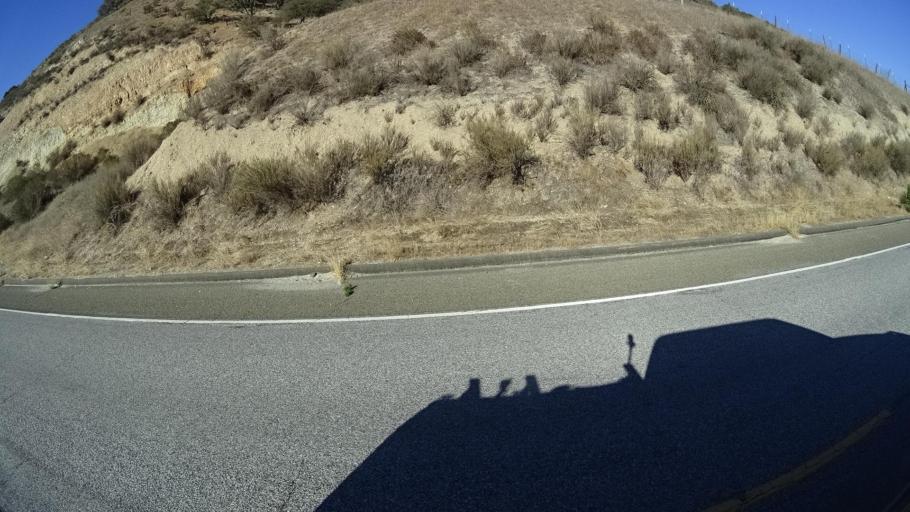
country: US
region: California
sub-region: Monterey County
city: King City
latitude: 36.1199
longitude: -121.1276
